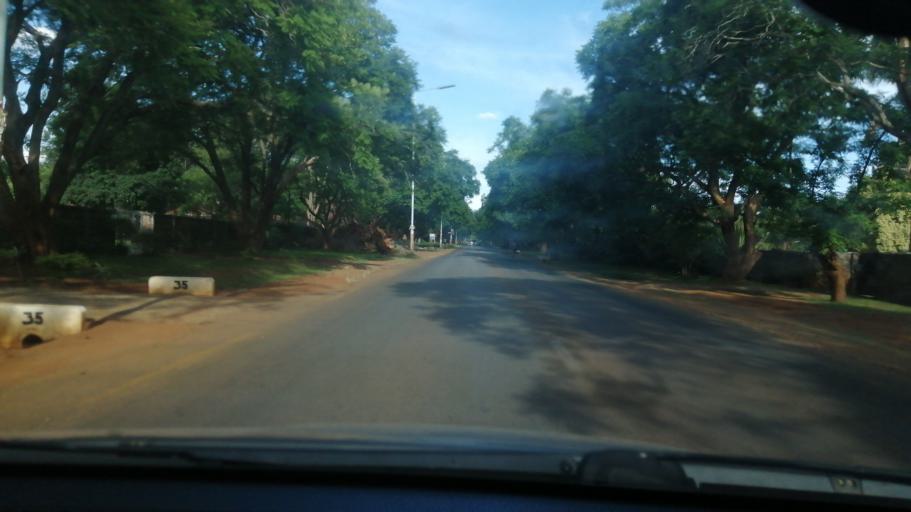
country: ZW
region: Harare
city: Harare
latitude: -17.7625
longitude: 31.0758
